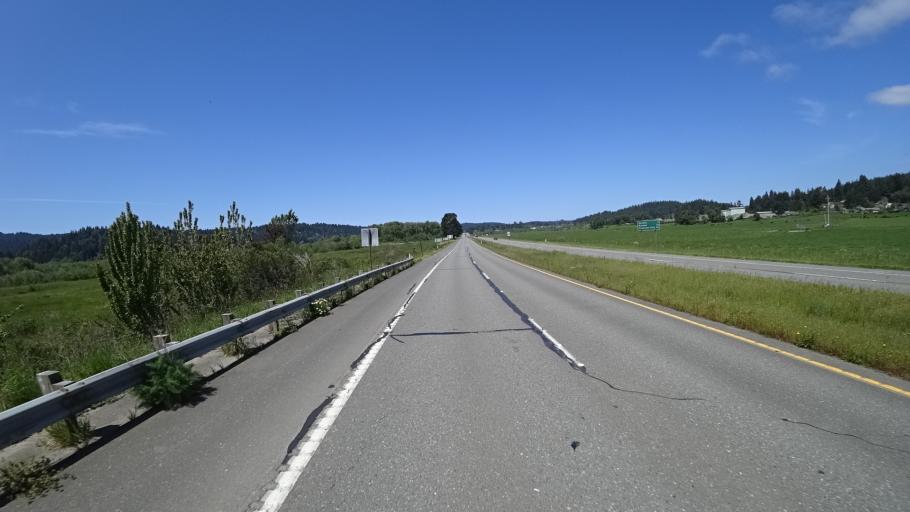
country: US
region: California
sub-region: Humboldt County
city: Blue Lake
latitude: 40.8897
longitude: -124.0052
